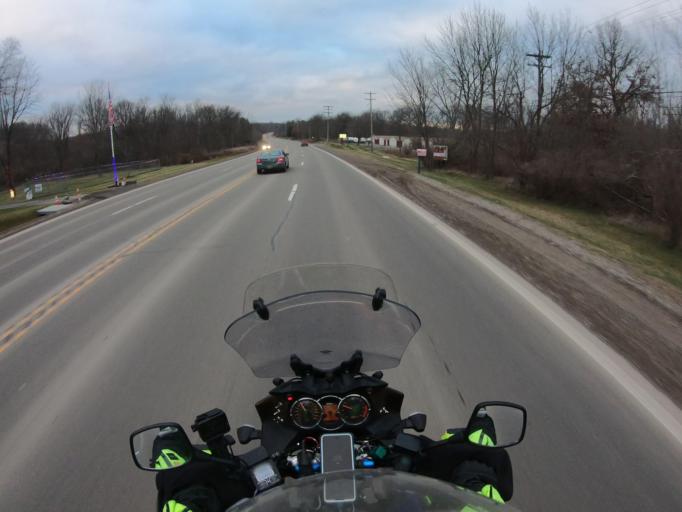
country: US
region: Michigan
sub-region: Oakland County
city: Holly
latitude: 42.8499
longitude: -83.5685
